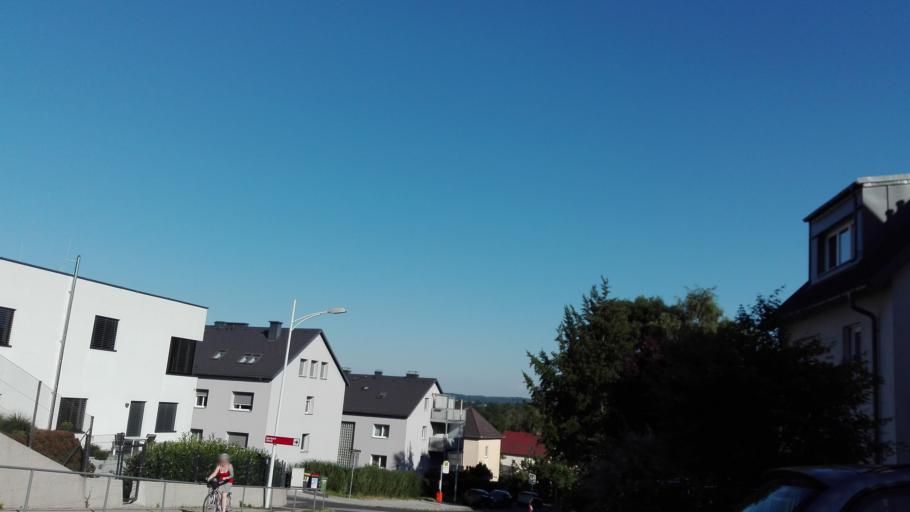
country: AT
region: Upper Austria
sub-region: Linz Stadt
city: Linz
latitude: 48.2697
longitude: 14.3002
